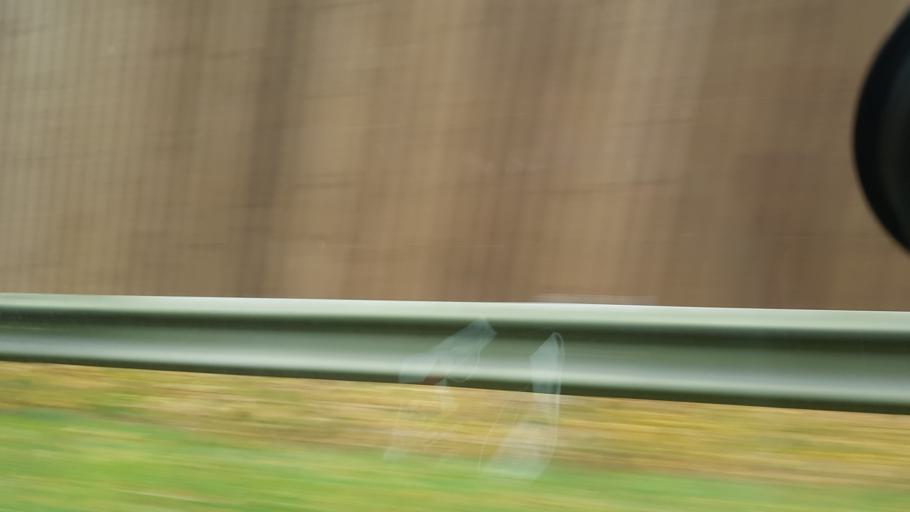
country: GB
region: England
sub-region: Hampshire
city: Fleet
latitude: 51.2952
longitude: -0.7995
